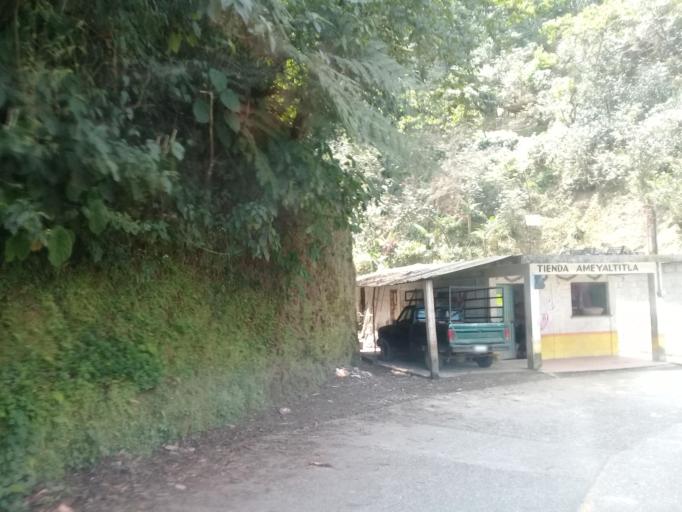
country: MX
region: Veracruz
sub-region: Tlilapan
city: Tonalixco
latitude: 18.7848
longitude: -97.0606
